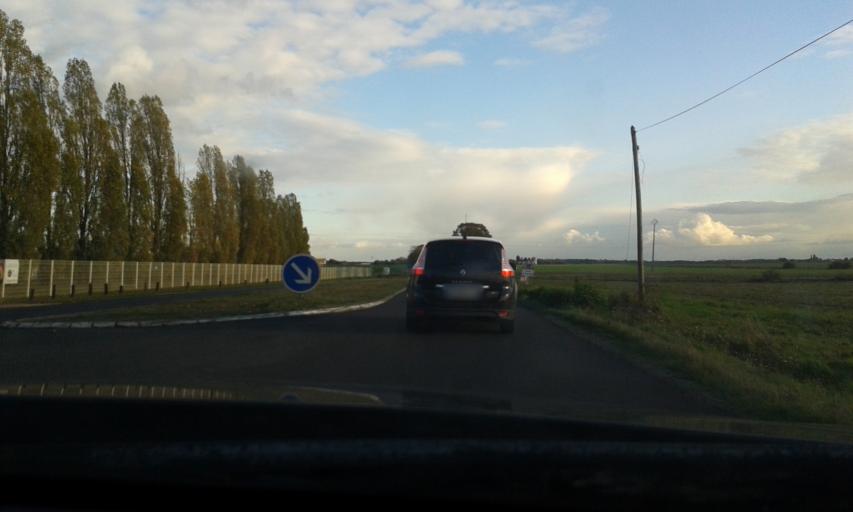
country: FR
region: Centre
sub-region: Departement d'Eure-et-Loir
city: Le Coudray
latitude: 48.4253
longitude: 1.5190
